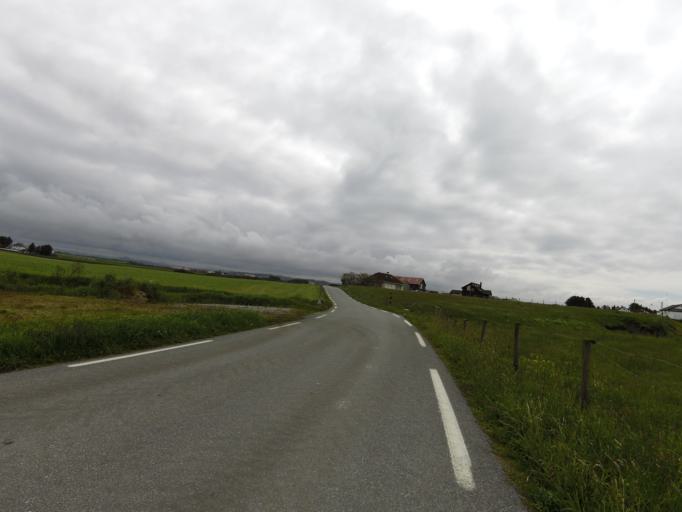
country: NO
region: Rogaland
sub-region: Klepp
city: Kleppe
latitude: 58.8114
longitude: 5.5534
